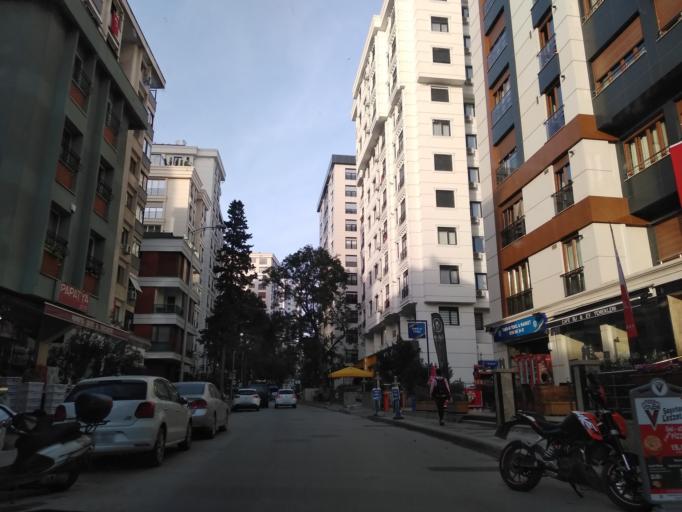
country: TR
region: Istanbul
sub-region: Atasehir
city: Atasehir
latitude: 40.9671
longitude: 29.0878
